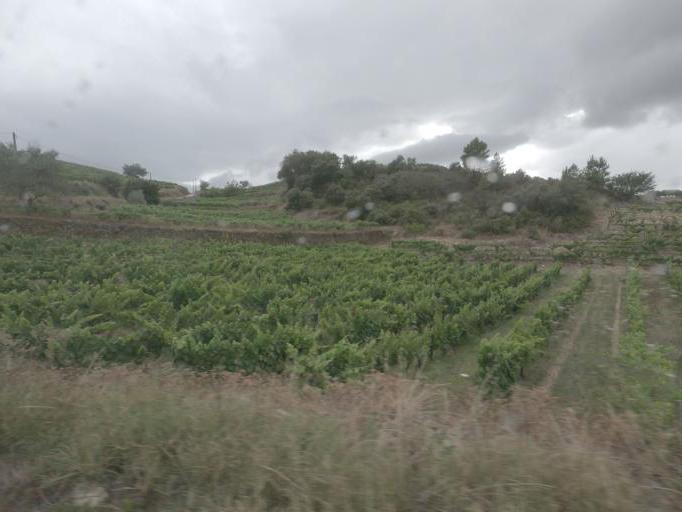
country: PT
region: Vila Real
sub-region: Sabrosa
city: Sabrosa
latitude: 41.2279
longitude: -7.5018
